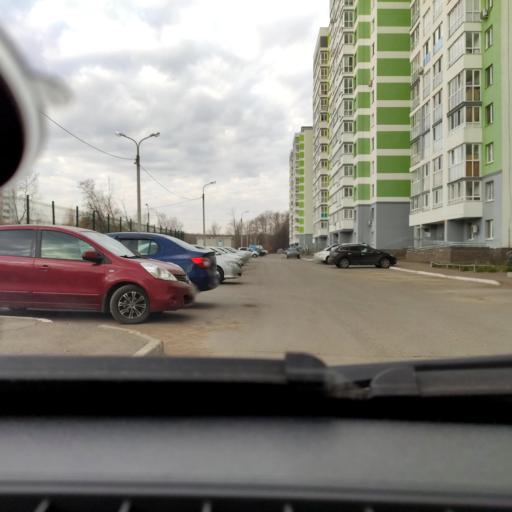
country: RU
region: Bashkortostan
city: Ufa
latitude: 54.7857
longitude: 56.1126
